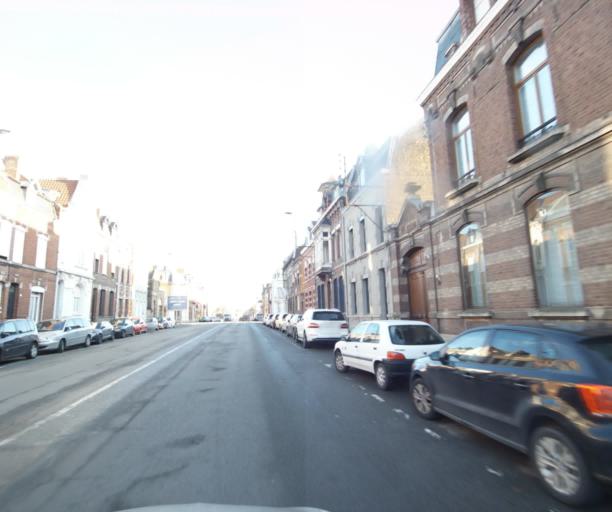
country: FR
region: Nord-Pas-de-Calais
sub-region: Departement du Nord
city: Valenciennes
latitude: 50.3536
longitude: 3.5312
